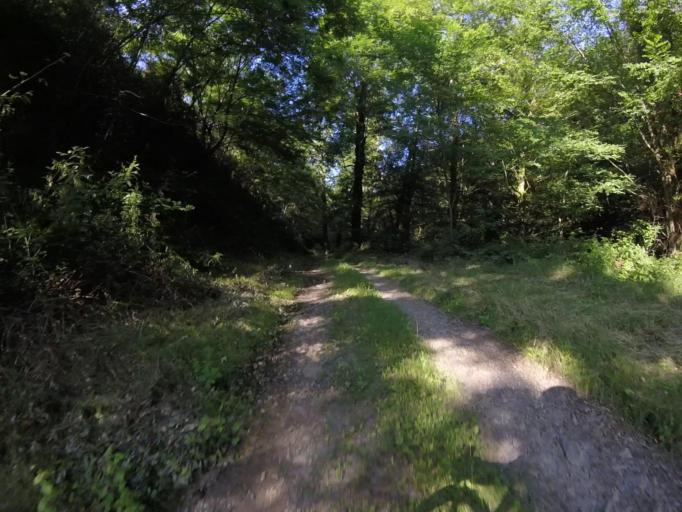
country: ES
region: Navarre
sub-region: Provincia de Navarra
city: Arano
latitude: 43.2472
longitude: -1.9036
